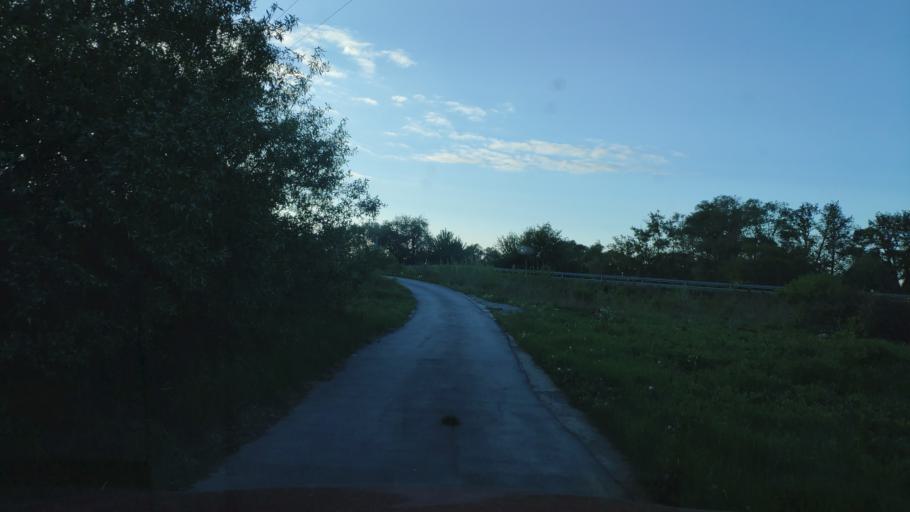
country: SK
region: Kosicky
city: Kosice
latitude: 48.7347
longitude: 21.4203
